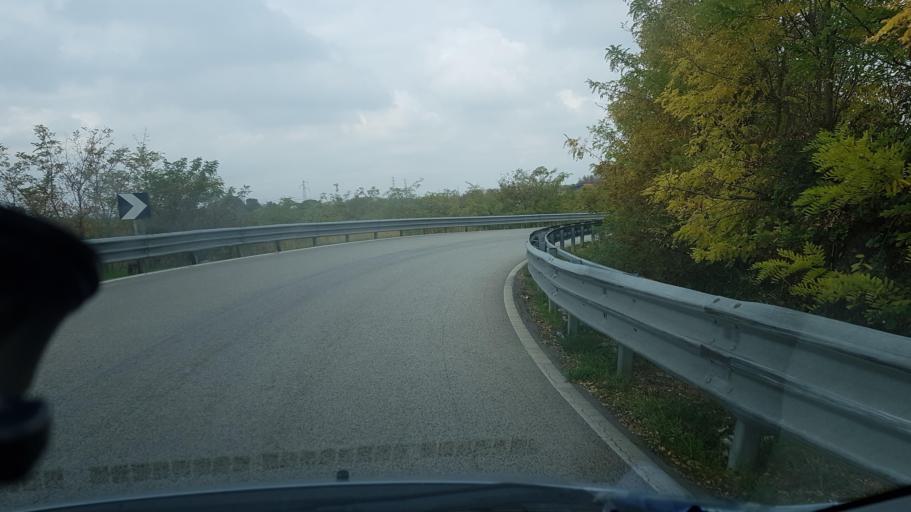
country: IT
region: Apulia
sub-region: Provincia di Foggia
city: Foggia
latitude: 41.4938
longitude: 15.5604
